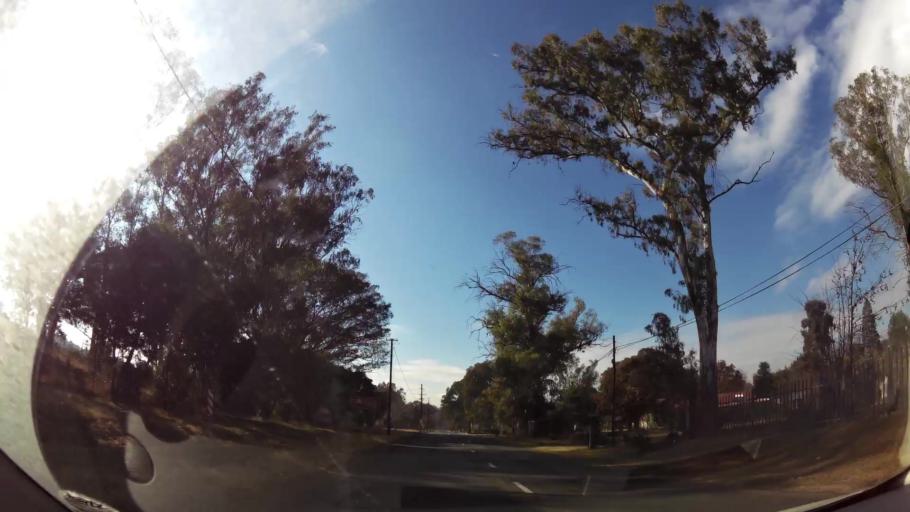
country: ZA
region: Gauteng
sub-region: Sedibeng District Municipality
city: Meyerton
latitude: -26.5284
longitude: 28.0630
